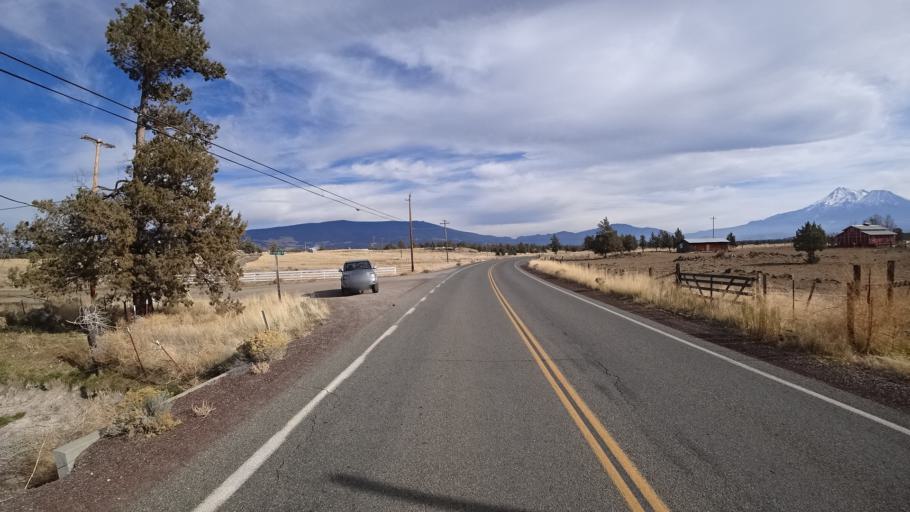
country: US
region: California
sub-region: Siskiyou County
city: Montague
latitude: 41.6241
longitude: -122.3814
